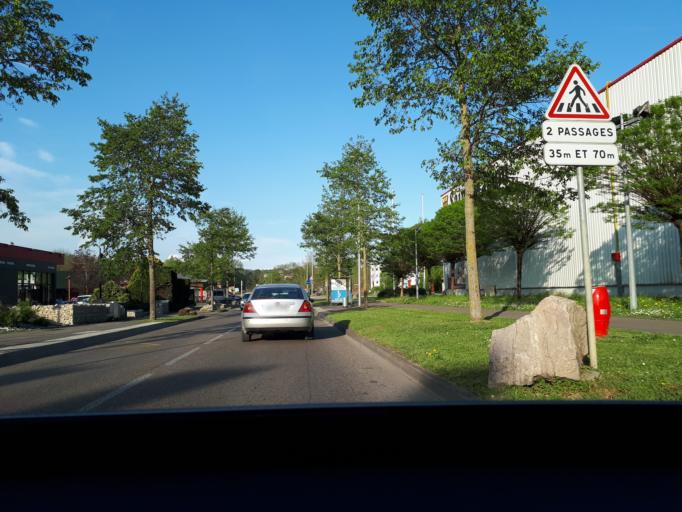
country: FR
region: Rhone-Alpes
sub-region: Departement de l'Isere
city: Domarin
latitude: 45.5889
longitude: 5.2560
